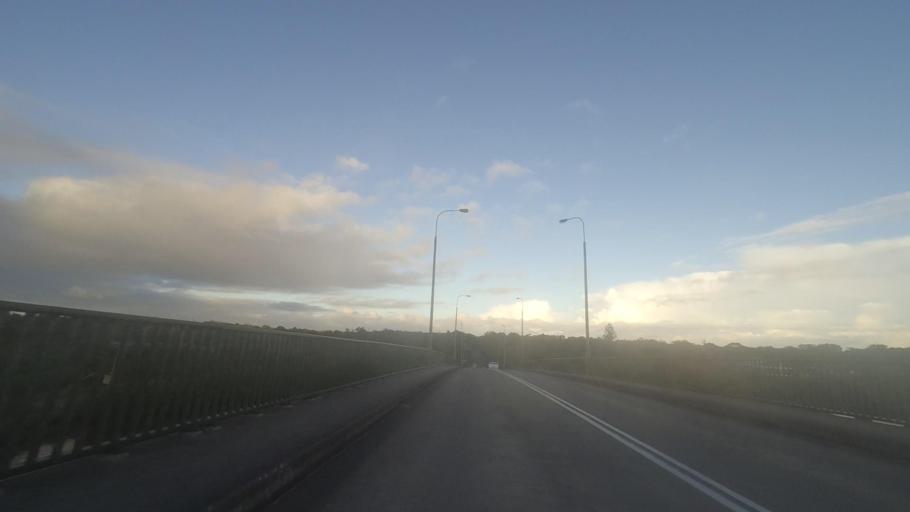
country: AU
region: New South Wales
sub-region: Great Lakes
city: Hawks Nest
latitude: -32.6691
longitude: 152.1685
